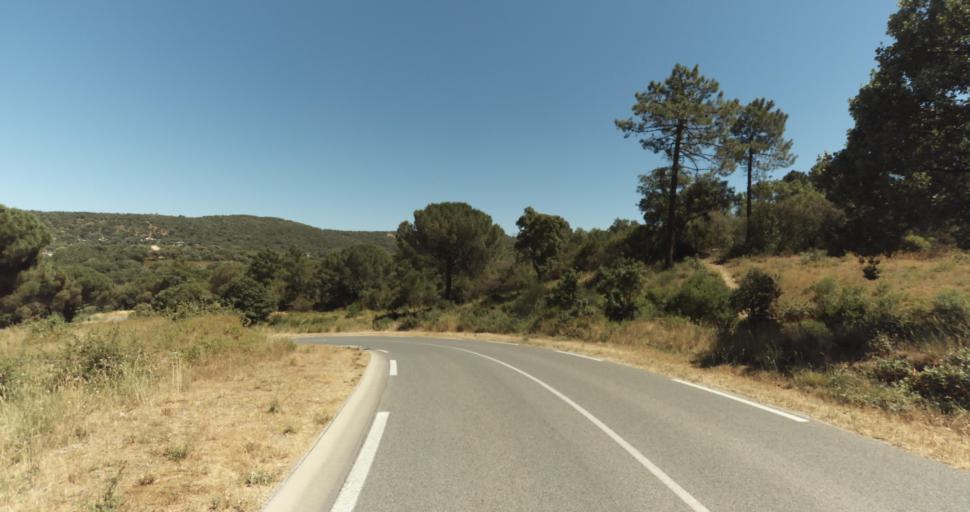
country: FR
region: Provence-Alpes-Cote d'Azur
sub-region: Departement du Var
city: Gassin
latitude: 43.2395
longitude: 6.5641
